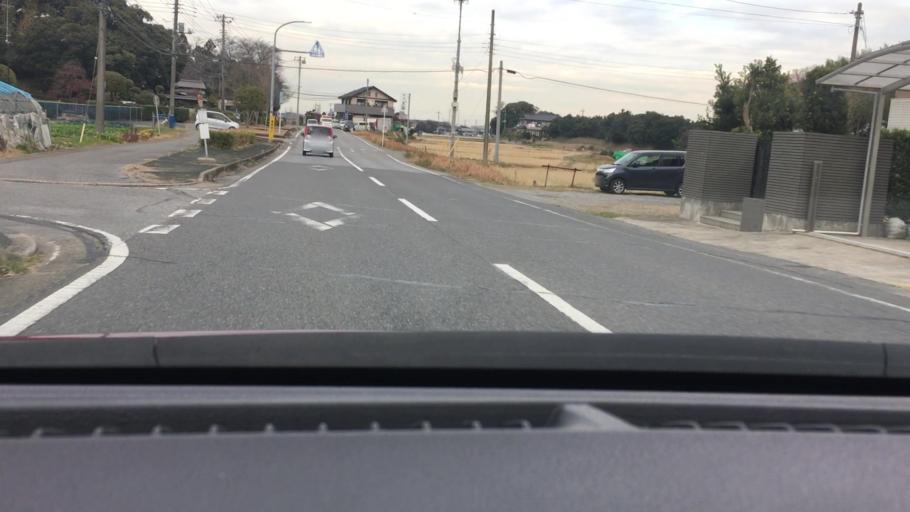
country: JP
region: Chiba
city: Ichihara
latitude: 35.4723
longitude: 140.0636
